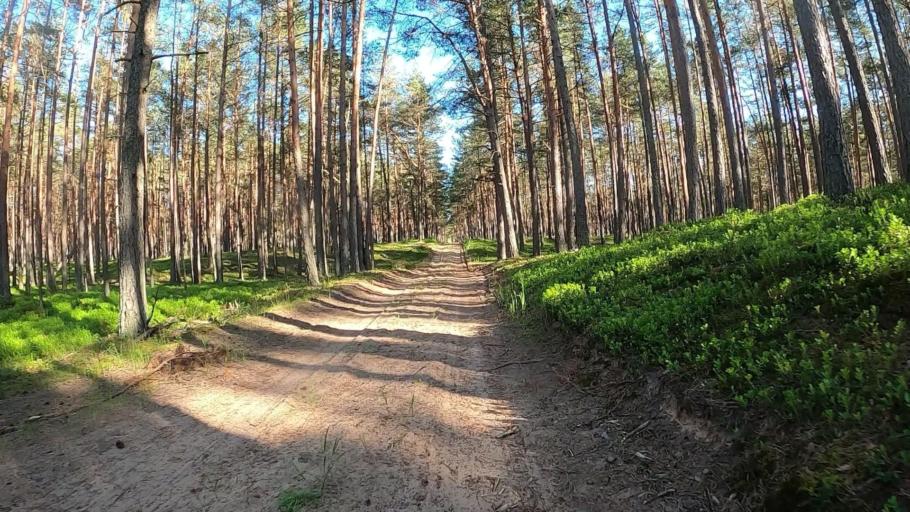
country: LV
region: Carnikava
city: Carnikava
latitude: 57.1098
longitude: 24.2437
